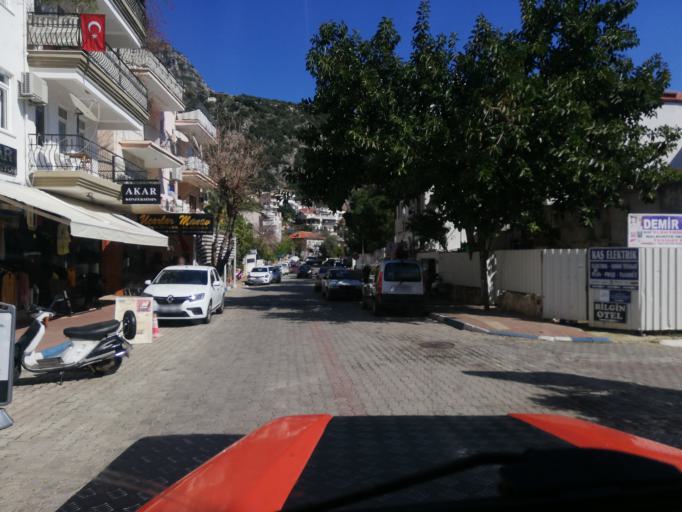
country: TR
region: Antalya
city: Kas
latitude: 36.2016
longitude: 29.6391
